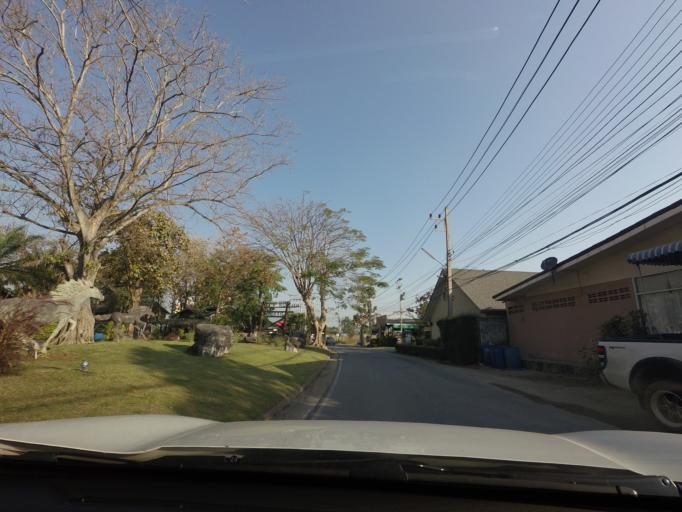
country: TH
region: Nakhon Ratchasima
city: Pak Chong
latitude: 14.5940
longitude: 101.4463
